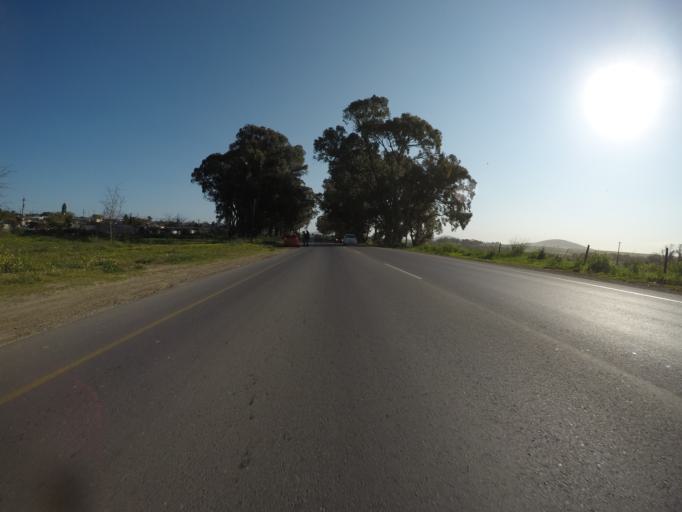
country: ZA
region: Western Cape
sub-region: City of Cape Town
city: Kraaifontein
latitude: -33.7796
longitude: 18.7186
